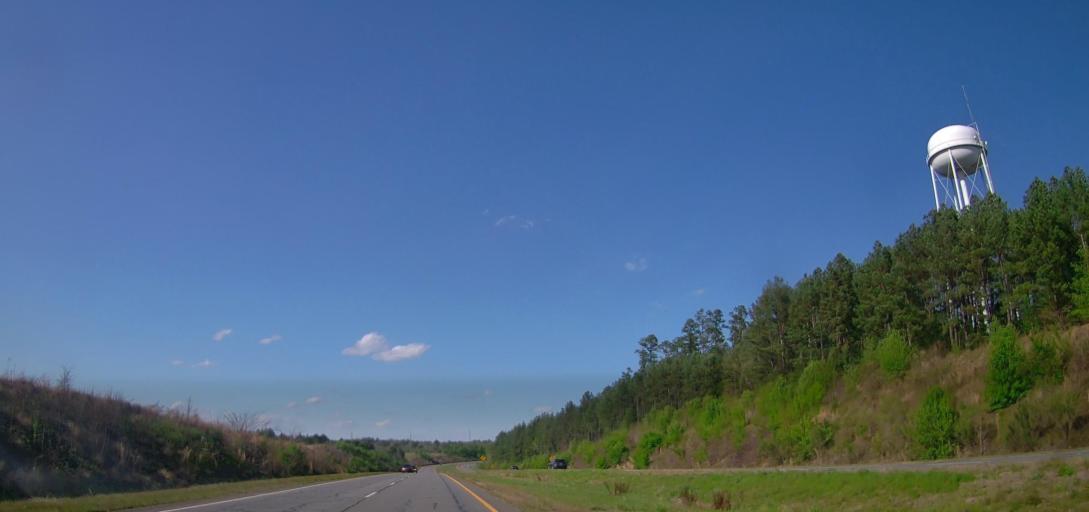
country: US
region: Georgia
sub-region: Baldwin County
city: Milledgeville
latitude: 33.0899
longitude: -83.2615
